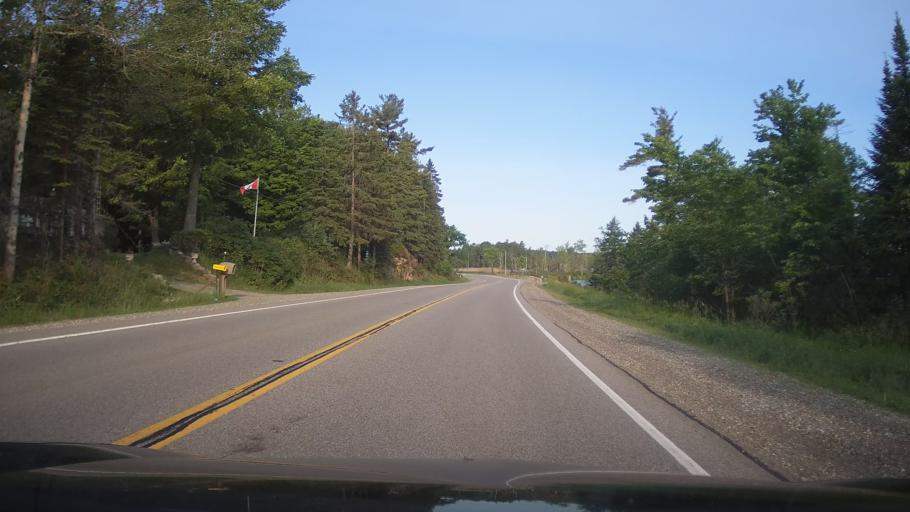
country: CA
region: Ontario
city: Perth
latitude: 44.8272
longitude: -76.5865
